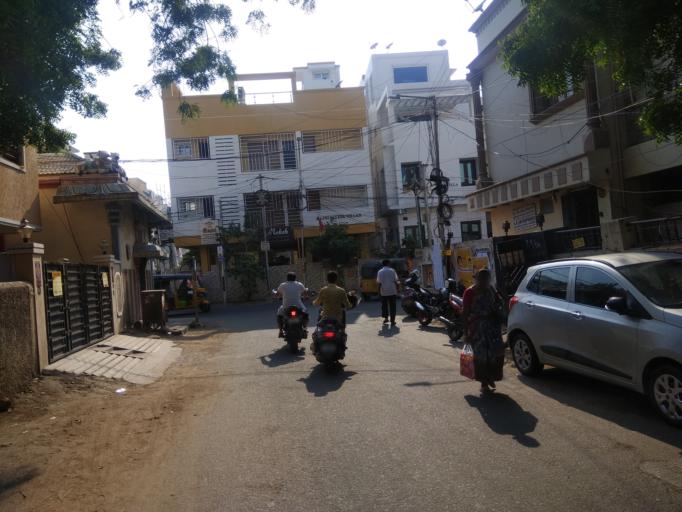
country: IN
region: Tamil Nadu
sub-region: Chennai
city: Gandhi Nagar
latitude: 13.0337
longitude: 80.2333
